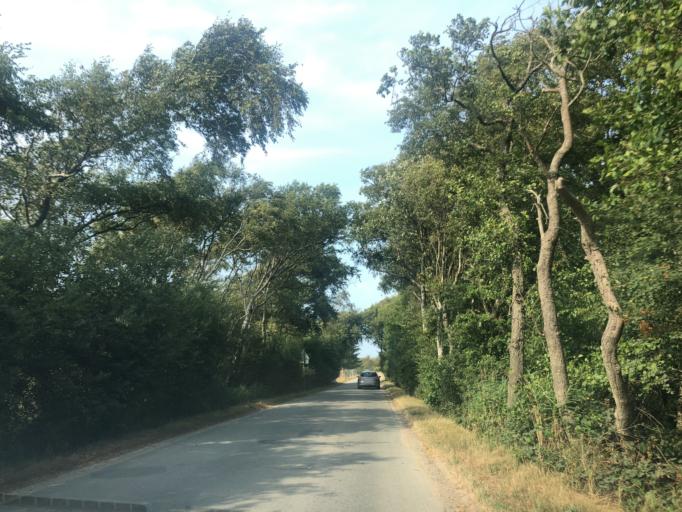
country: DK
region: North Denmark
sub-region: Morso Kommune
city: Nykobing Mors
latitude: 56.8344
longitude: 9.0452
